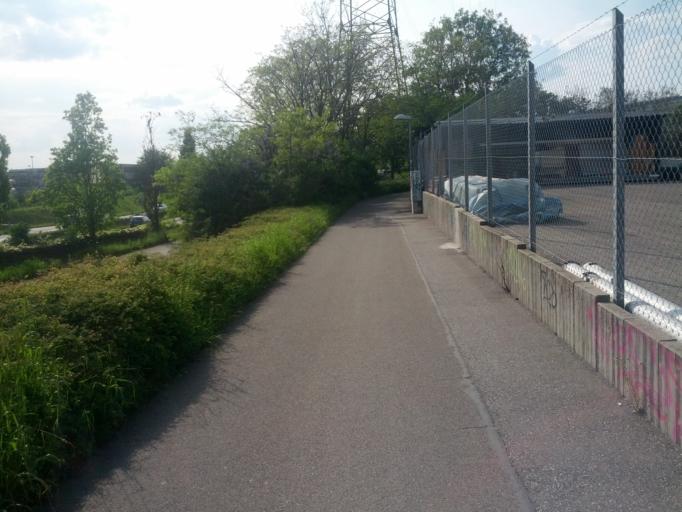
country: DE
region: Baden-Wuerttemberg
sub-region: Freiburg Region
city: Merzhausen
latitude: 47.9844
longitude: 7.8079
